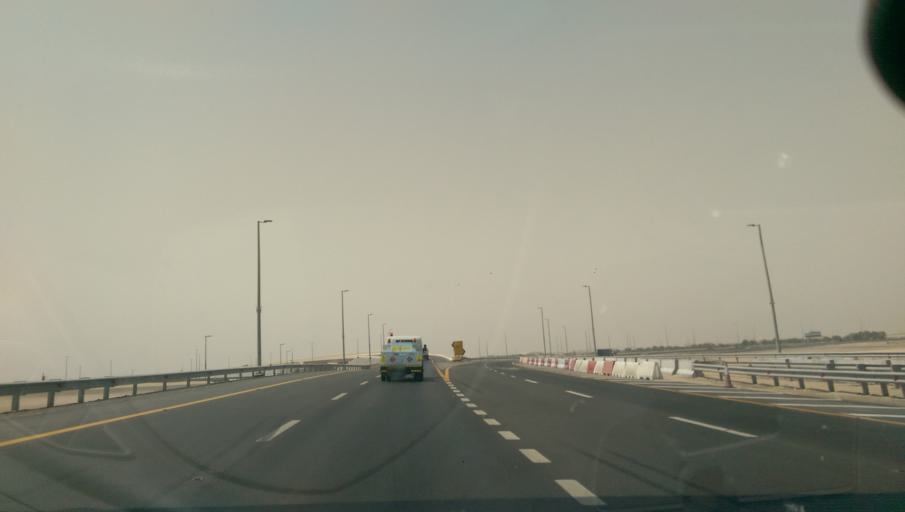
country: AE
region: Abu Dhabi
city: Abu Dhabi
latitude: 24.2903
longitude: 54.5479
